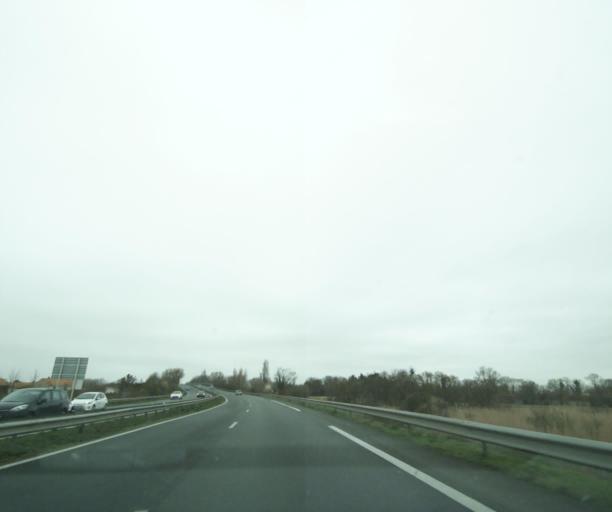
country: FR
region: Poitou-Charentes
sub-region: Departement de la Charente-Maritime
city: Yves
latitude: 46.0378
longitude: -1.0479
